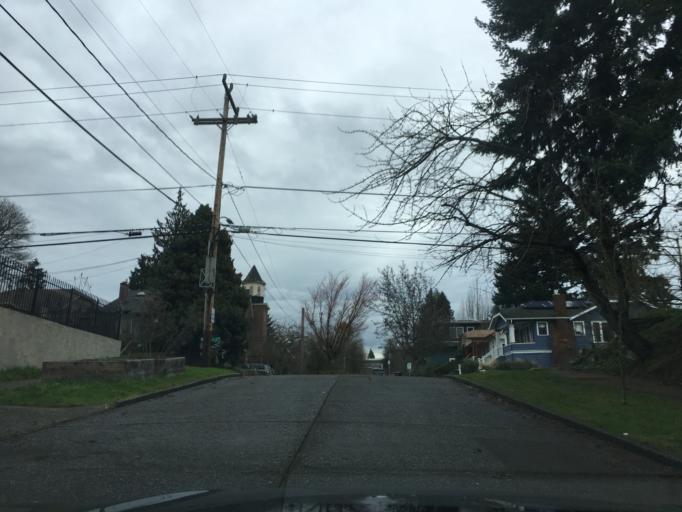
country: US
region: Washington
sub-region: King County
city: Seattle
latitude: 47.6580
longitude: -122.3413
